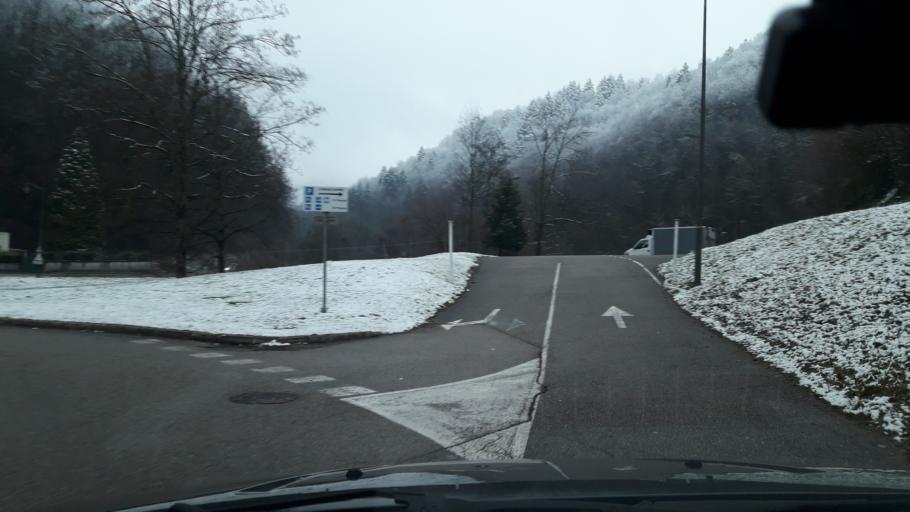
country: FR
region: Rhone-Alpes
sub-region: Departement de l'Isere
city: Vaulnaveys-le-Haut
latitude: 45.1450
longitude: 5.8292
